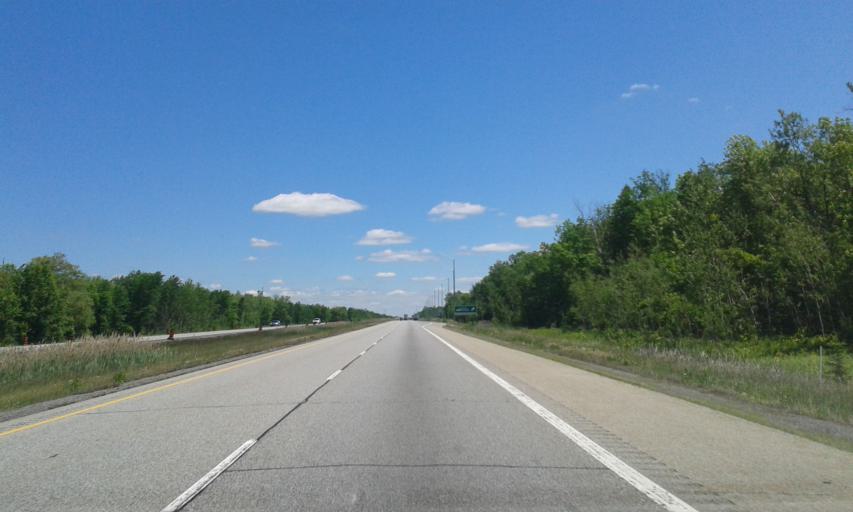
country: US
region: New York
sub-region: St. Lawrence County
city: Norfolk
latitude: 44.9407
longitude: -75.1412
